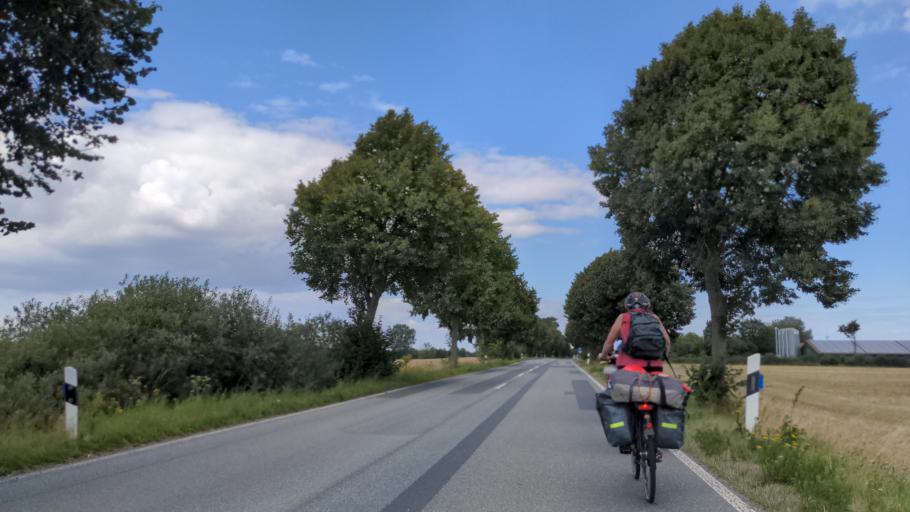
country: DE
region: Schleswig-Holstein
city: Beschendorf
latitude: 54.1710
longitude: 10.8738
